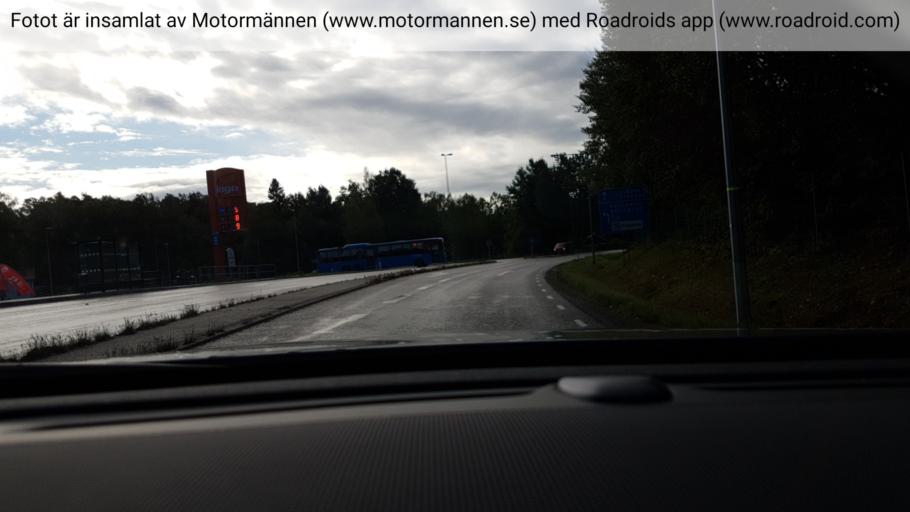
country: SE
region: Vaestra Goetaland
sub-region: Harryda Kommun
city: Ravlanda
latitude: 57.6195
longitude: 12.4342
